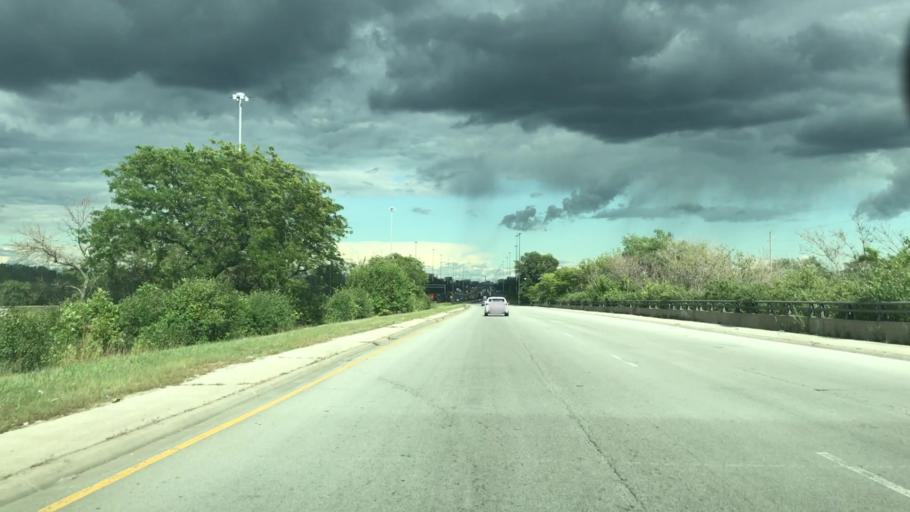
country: US
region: Illinois
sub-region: Cook County
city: Summit
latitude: 41.7987
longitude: -87.8011
